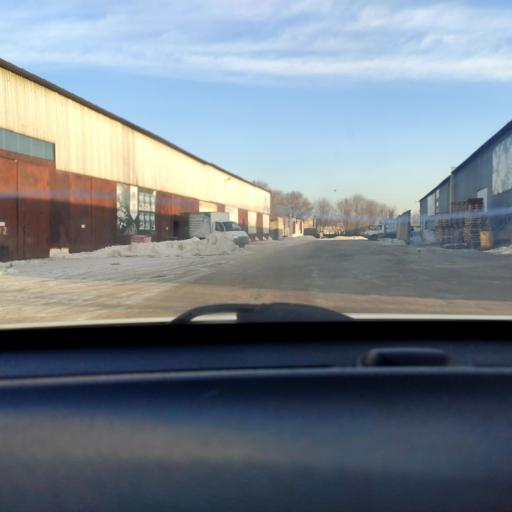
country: RU
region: Voronezj
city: Voronezh
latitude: 51.6579
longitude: 39.2696
